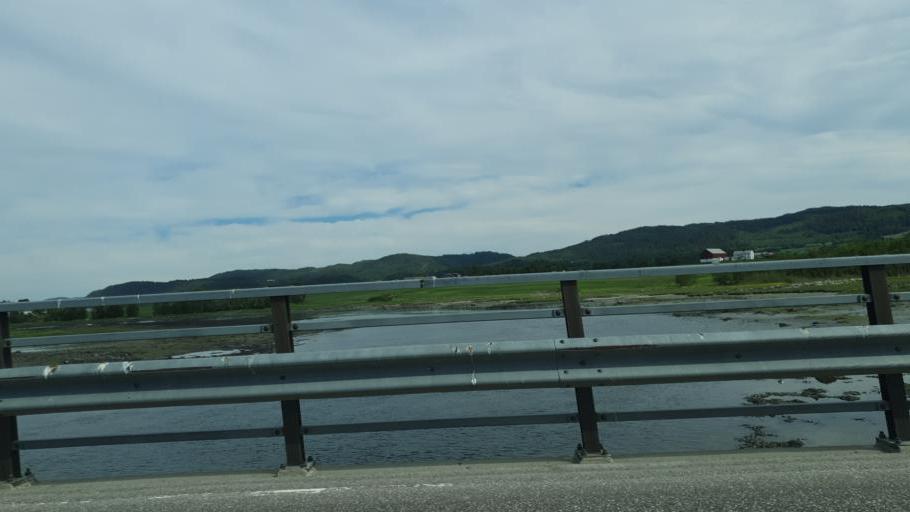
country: NO
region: Sor-Trondelag
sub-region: Rissa
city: Rissa
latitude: 63.5772
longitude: 9.9350
